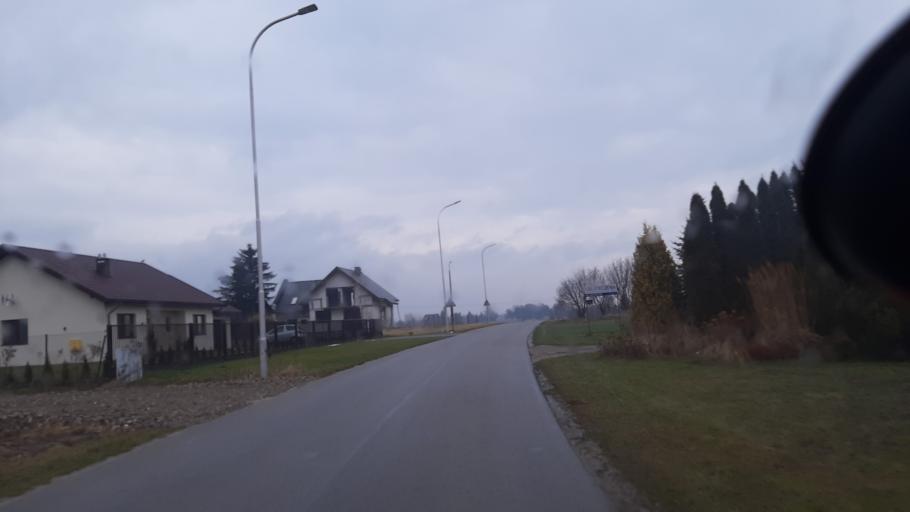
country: PL
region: Lublin Voivodeship
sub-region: Powiat lubelski
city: Niemce
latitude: 51.3302
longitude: 22.5876
